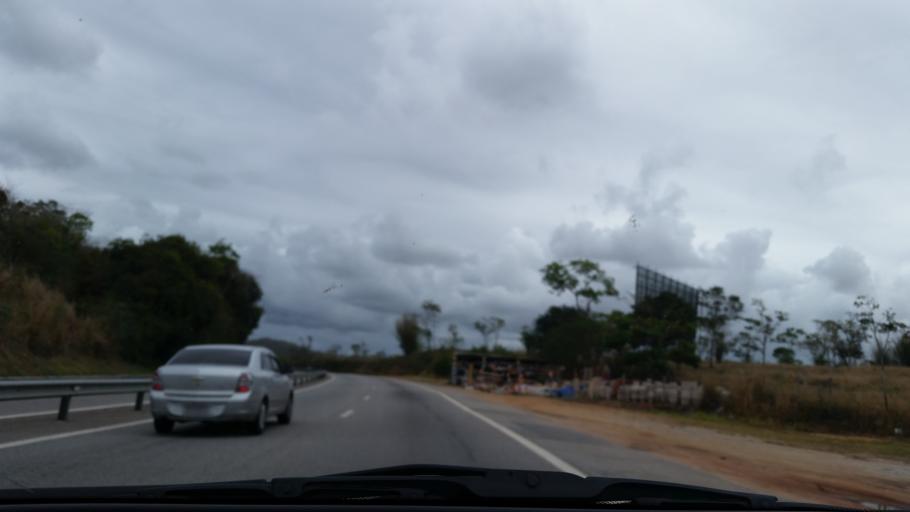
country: BR
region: Rio de Janeiro
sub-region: Araruama
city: Araruama
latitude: -22.8027
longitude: -42.4084
